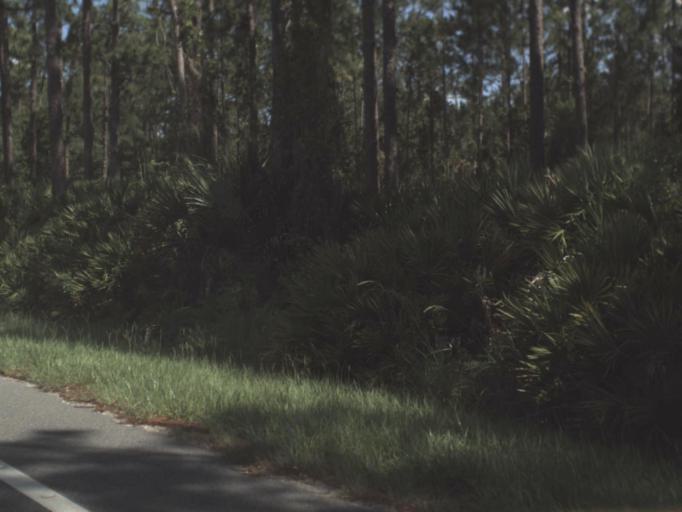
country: US
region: Florida
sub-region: Putnam County
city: Palatka
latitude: 29.6834
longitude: -81.7316
